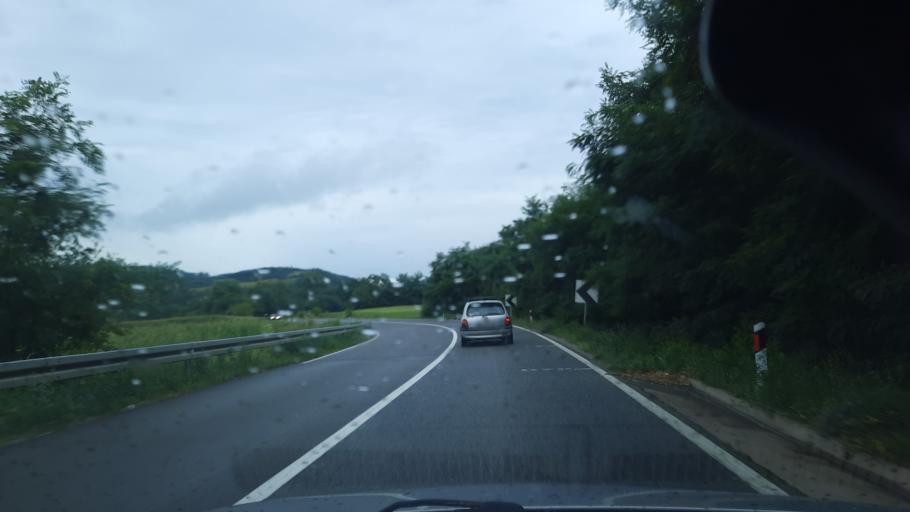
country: RS
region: Central Serbia
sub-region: Sumadijski Okrug
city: Knic
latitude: 43.8601
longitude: 20.7771
